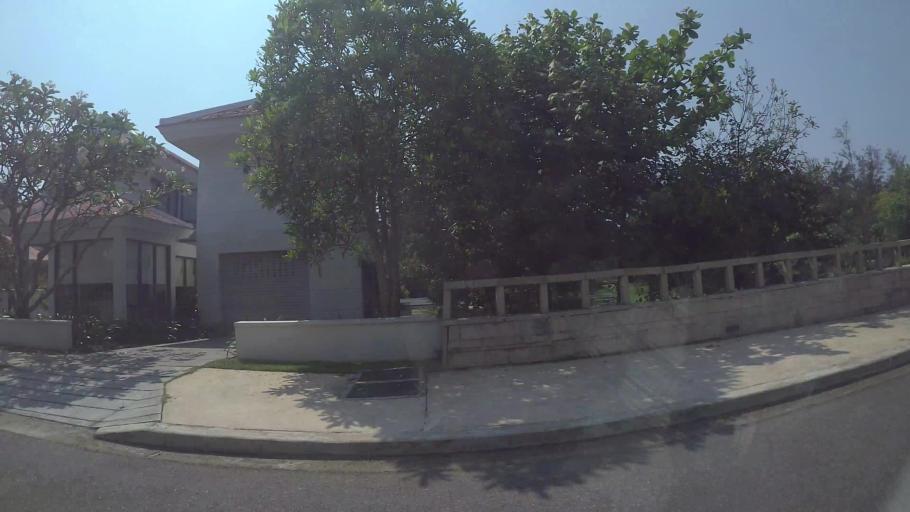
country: VN
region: Da Nang
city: Ngu Hanh Son
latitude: 15.9776
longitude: 108.2815
